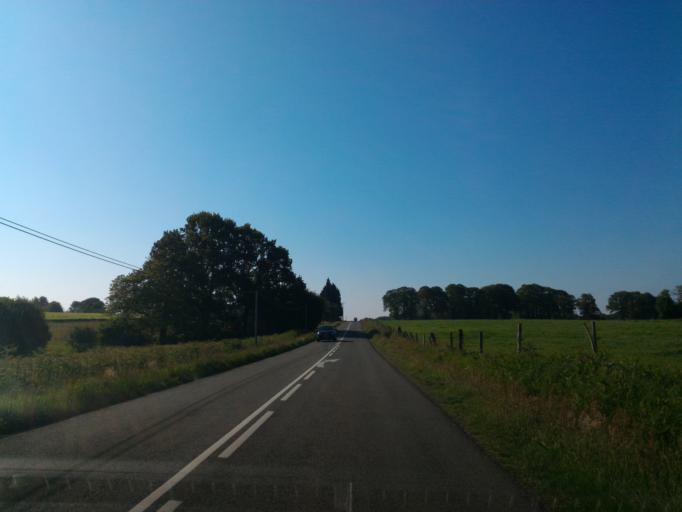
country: FR
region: Brittany
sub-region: Departement d'Ille-et-Vilaine
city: Luitre
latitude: 48.2512
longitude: -1.1243
